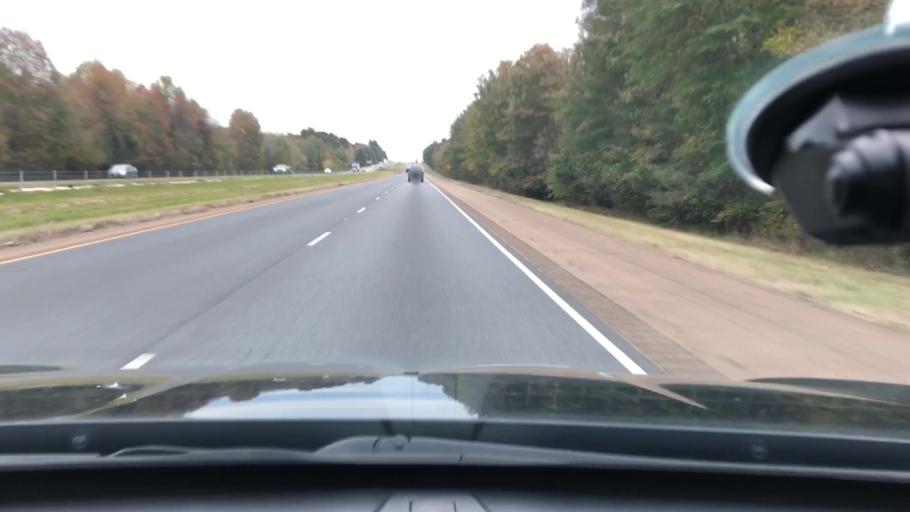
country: US
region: Arkansas
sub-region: Clark County
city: Gurdon
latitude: 33.9841
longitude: -93.1963
